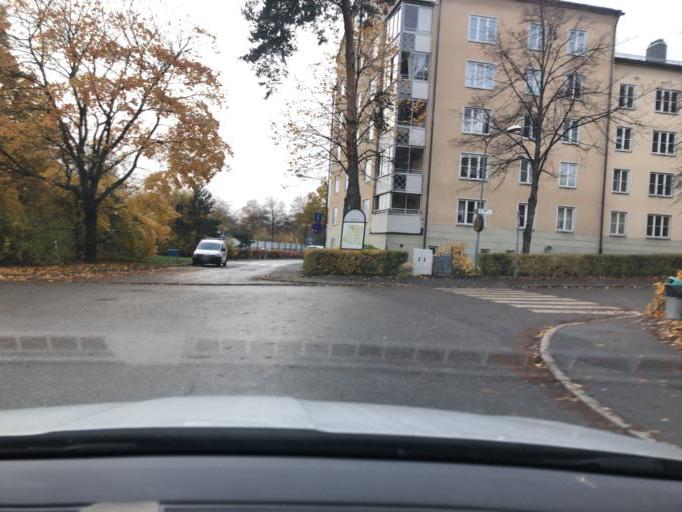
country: SE
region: Stockholm
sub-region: Stockholms Kommun
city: Arsta
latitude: 59.2873
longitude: 18.0804
